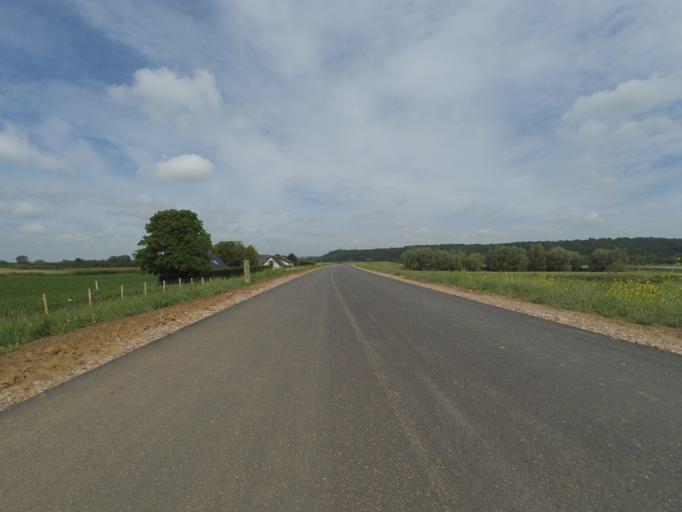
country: NL
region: Utrecht
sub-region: Gemeente Rhenen
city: Rhenen
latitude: 51.9427
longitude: 5.5982
